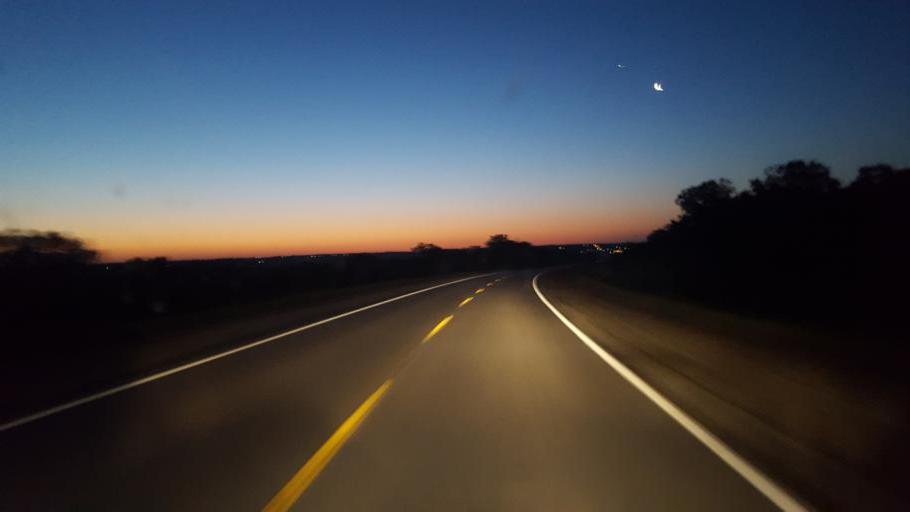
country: US
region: Missouri
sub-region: Mercer County
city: Princeton
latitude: 40.4025
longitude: -93.6308
